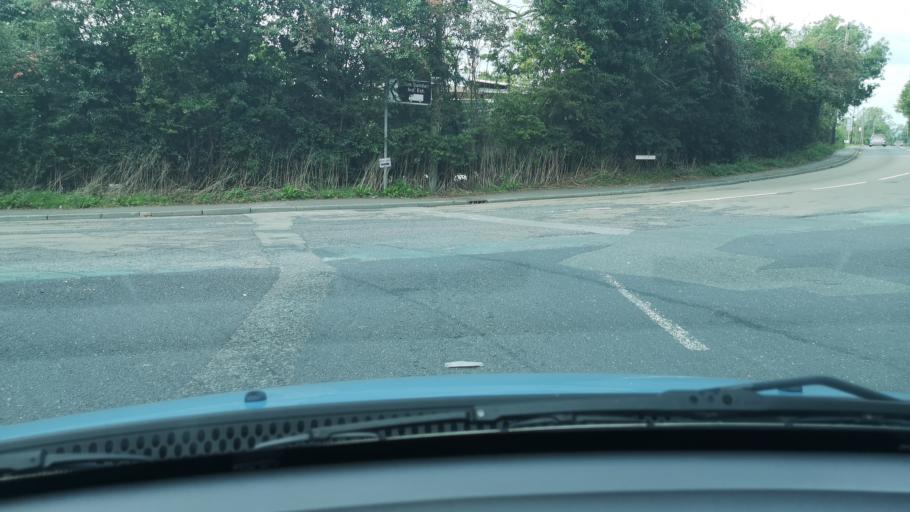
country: GB
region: England
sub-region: Doncaster
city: Kirk Sandall
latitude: 53.5698
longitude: -1.0652
